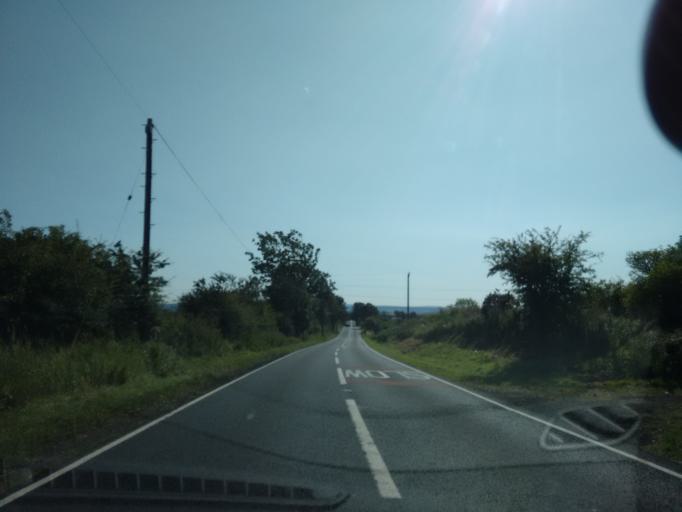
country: GB
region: England
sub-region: Northumberland
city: Corbridge
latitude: 55.0112
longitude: -2.0209
